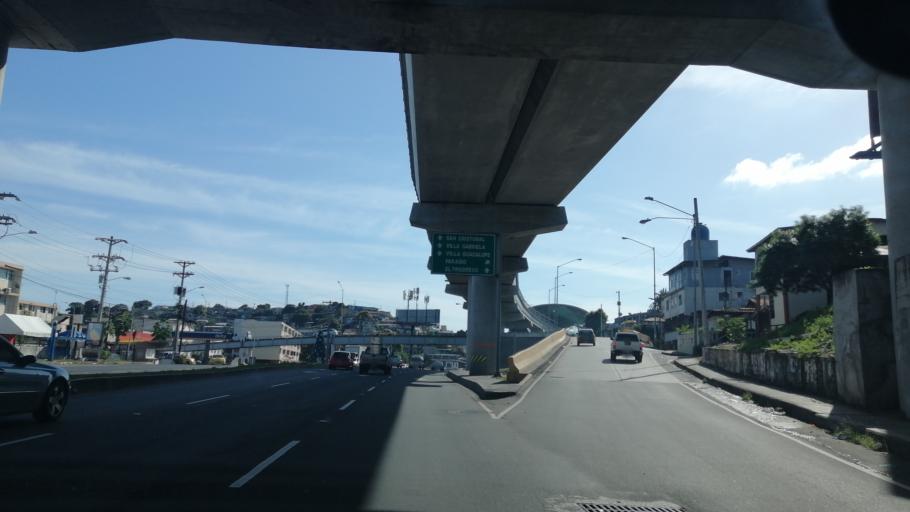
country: PA
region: Panama
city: San Miguelito
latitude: 9.0306
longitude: -79.5016
